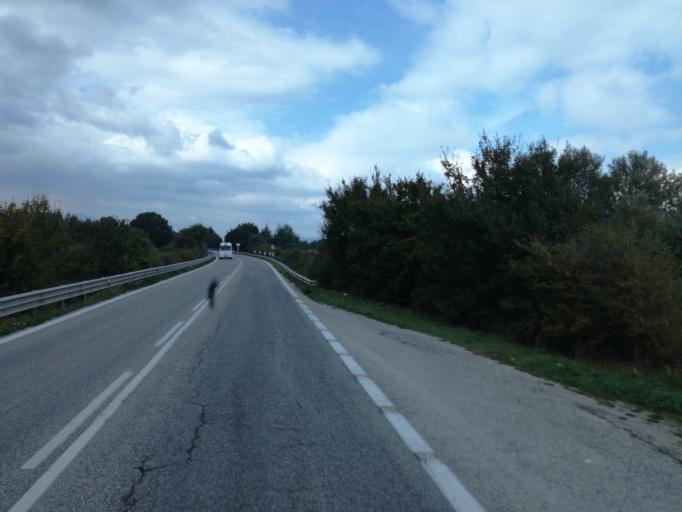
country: IT
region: Molise
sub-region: Provincia di Campobasso
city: Guardiaregia
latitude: 41.4677
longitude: 14.5484
